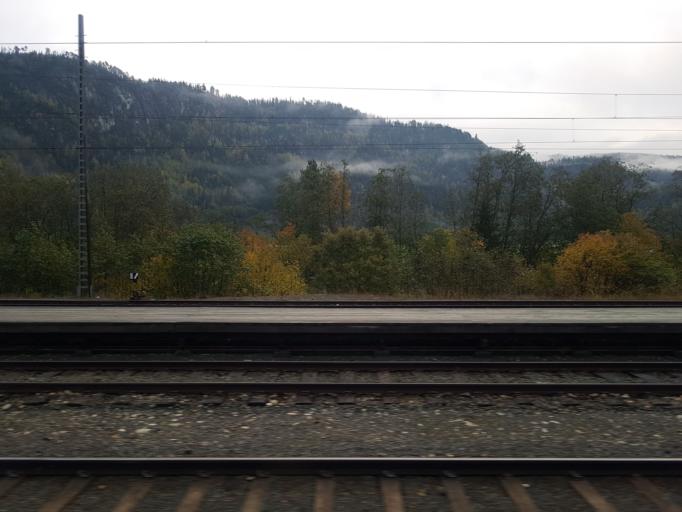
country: NO
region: Sor-Trondelag
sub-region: Midtre Gauldal
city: Storen
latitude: 63.0401
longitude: 10.2841
